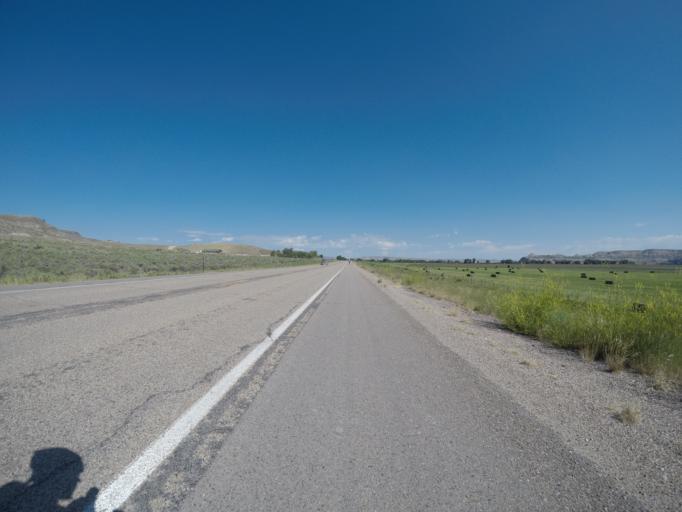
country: US
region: Wyoming
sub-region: Sublette County
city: Marbleton
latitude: 42.2064
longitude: -110.1828
